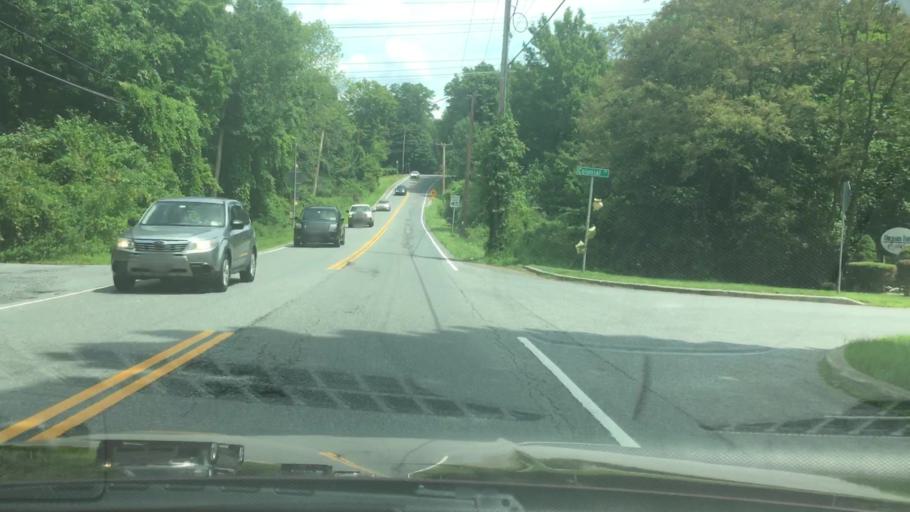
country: US
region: New York
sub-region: Dutchess County
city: Red Oaks Mill
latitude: 41.6520
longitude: -73.8352
